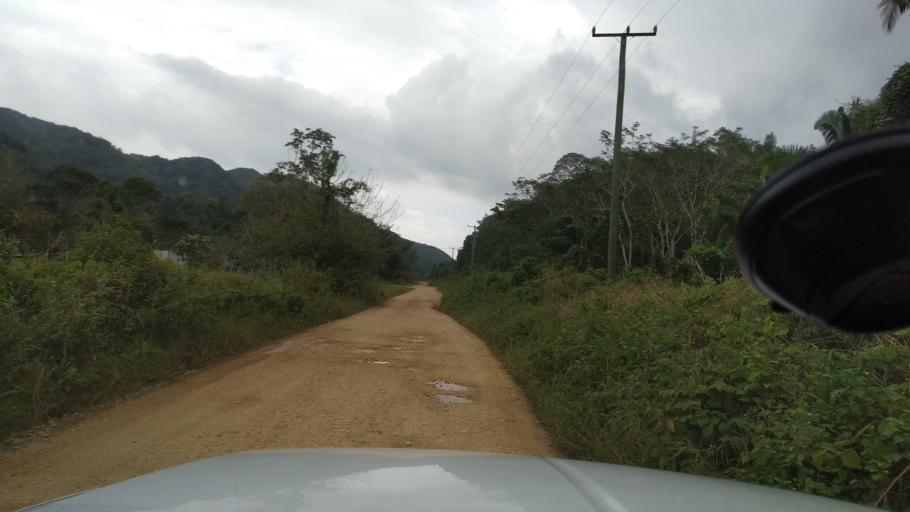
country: BZ
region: Toledo
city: Punta Gorda
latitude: 16.2060
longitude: -89.0293
